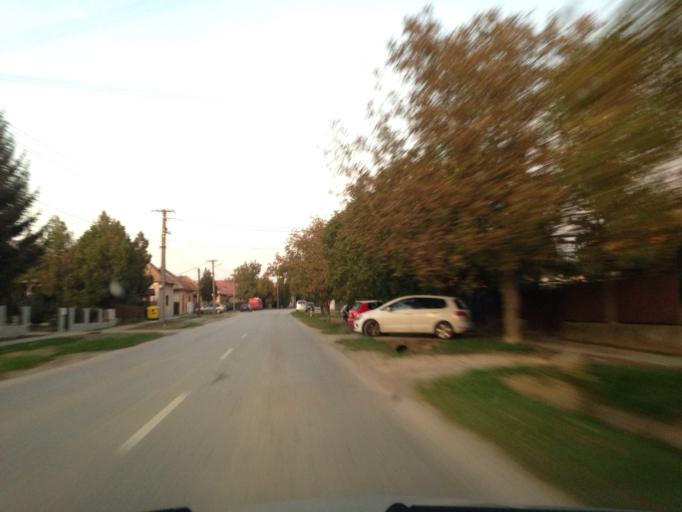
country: SK
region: Nitriansky
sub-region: Okres Komarno
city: Hurbanovo
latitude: 47.8439
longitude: 18.2604
